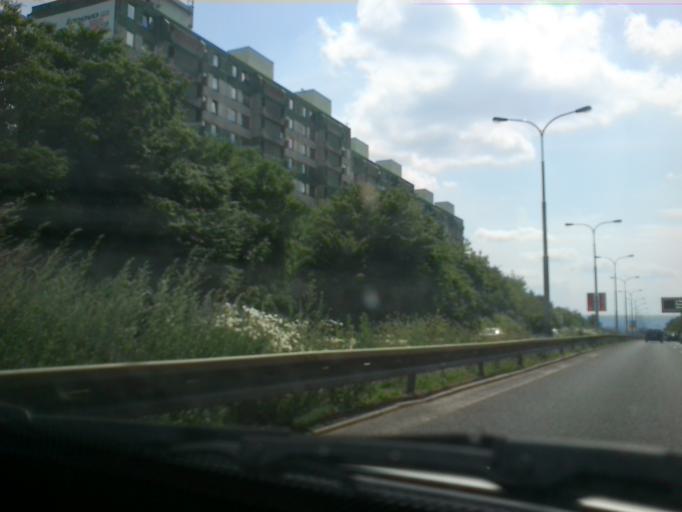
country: CZ
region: Praha
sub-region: Praha 9
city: Strizkov
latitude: 50.1270
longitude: 14.4836
